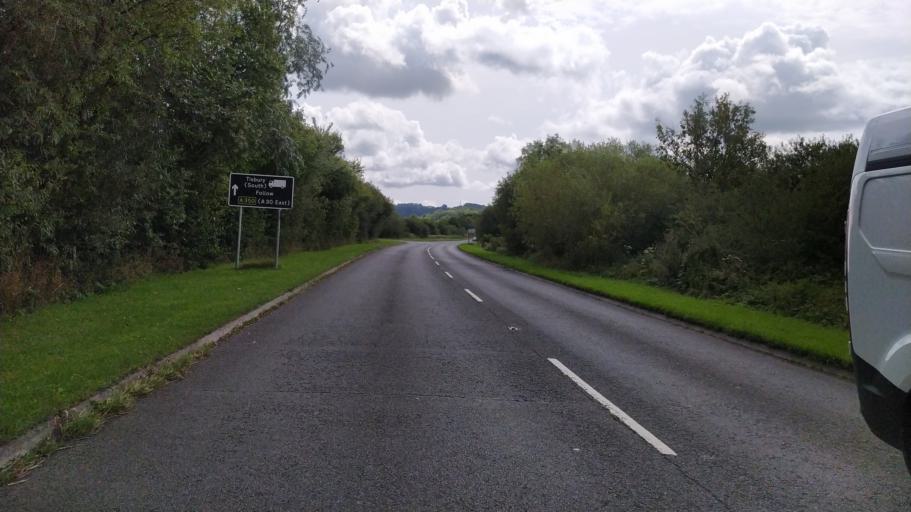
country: GB
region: England
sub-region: Dorset
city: Shaftesbury
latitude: 51.0471
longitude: -2.1837
